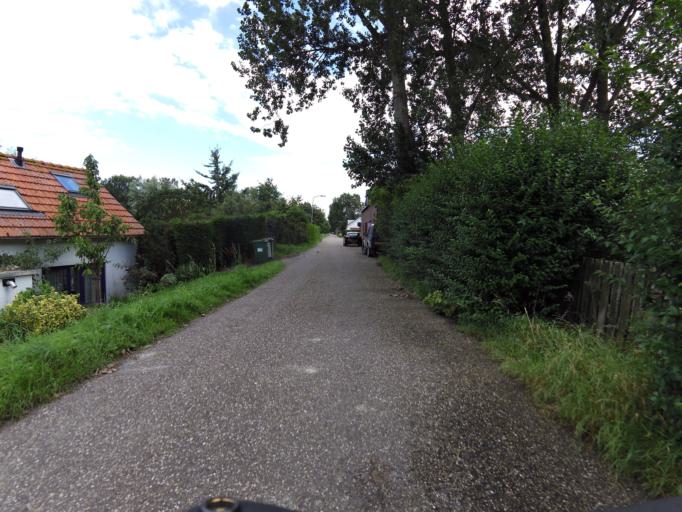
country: NL
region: South Holland
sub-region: Gemeente Goeree-Overflakkee
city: Middelharnis
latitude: 51.6976
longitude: 4.2634
